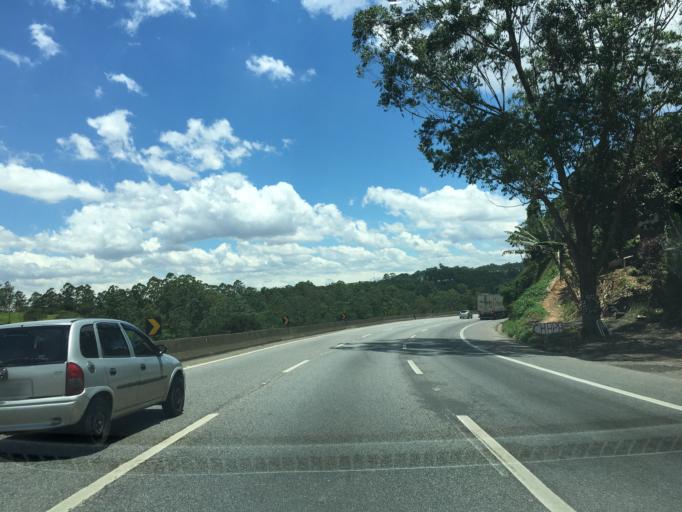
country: BR
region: Sao Paulo
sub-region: Guarulhos
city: Guarulhos
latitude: -23.4026
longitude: -46.5756
